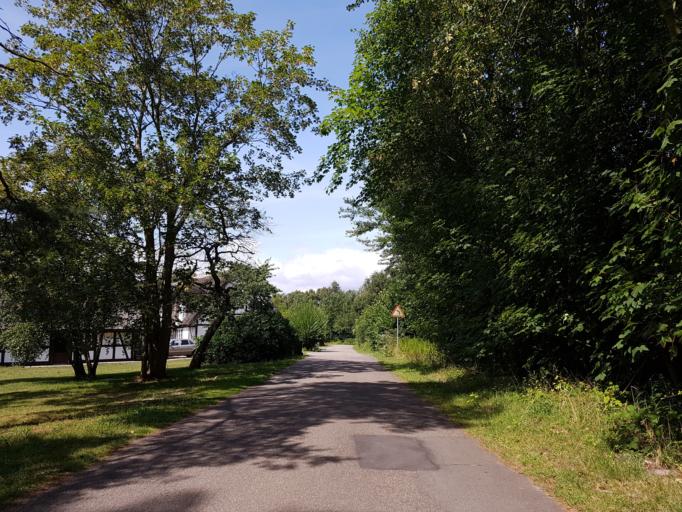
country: DK
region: Zealand
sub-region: Guldborgsund Kommune
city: Nykobing Falster
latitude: 54.6052
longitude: 11.9579
